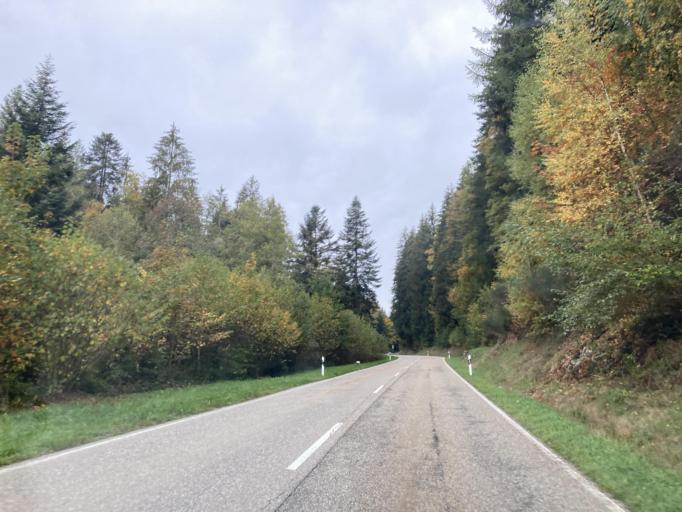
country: DE
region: Baden-Wuerttemberg
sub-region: Karlsruhe Region
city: Forbach
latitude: 48.6484
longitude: 8.3362
